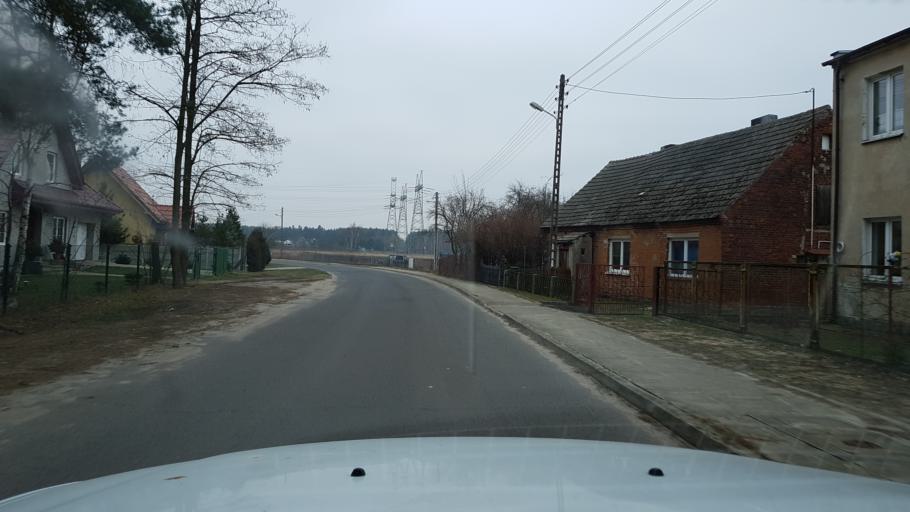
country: PL
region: West Pomeranian Voivodeship
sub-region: Powiat gryfinski
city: Gryfino
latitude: 53.1960
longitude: 14.4837
